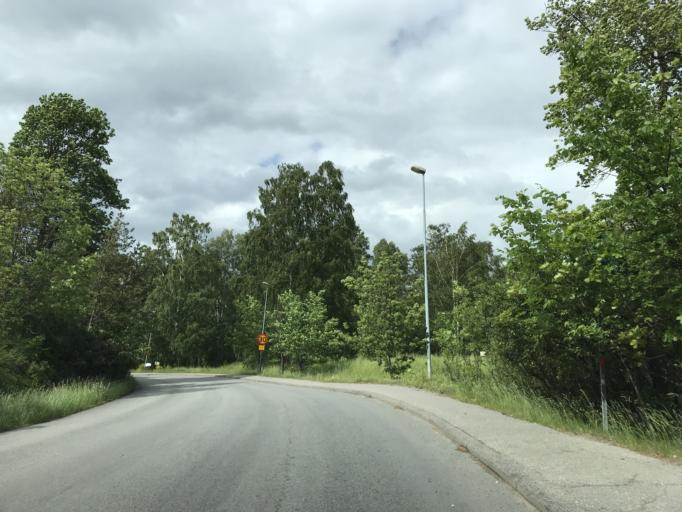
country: SE
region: Stockholm
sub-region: Norrtalje Kommun
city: Bergshamra
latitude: 59.3820
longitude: 18.0107
